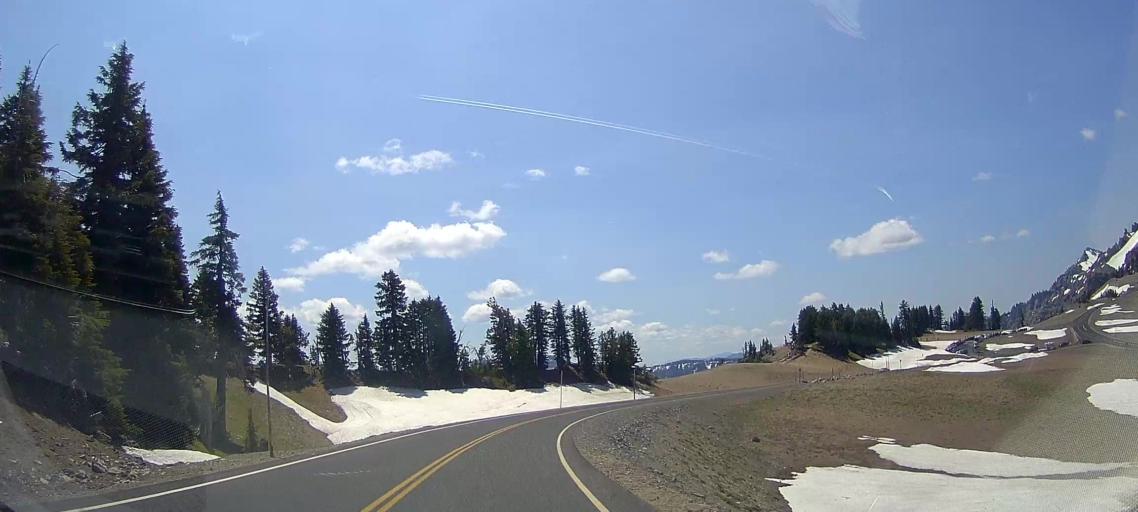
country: US
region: Oregon
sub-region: Jackson County
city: Shady Cove
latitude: 42.9682
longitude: -122.1496
